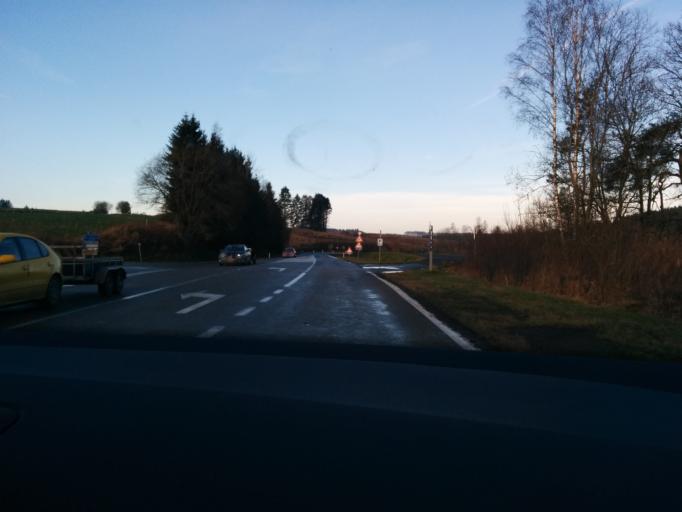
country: BE
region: Wallonia
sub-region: Province du Luxembourg
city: Gouvy
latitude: 50.2226
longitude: 5.9385
